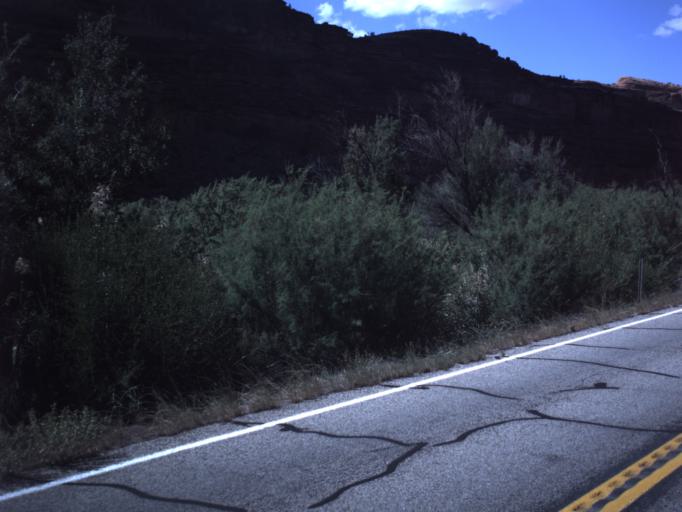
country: US
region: Utah
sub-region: Grand County
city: Moab
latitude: 38.5387
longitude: -109.6304
